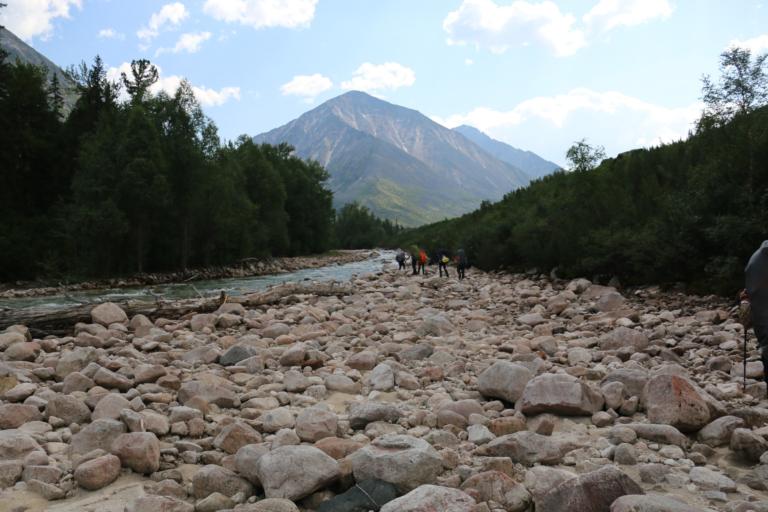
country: RU
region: Respublika Buryatiya
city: Novyy Uoyan
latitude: 56.2974
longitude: 111.1357
